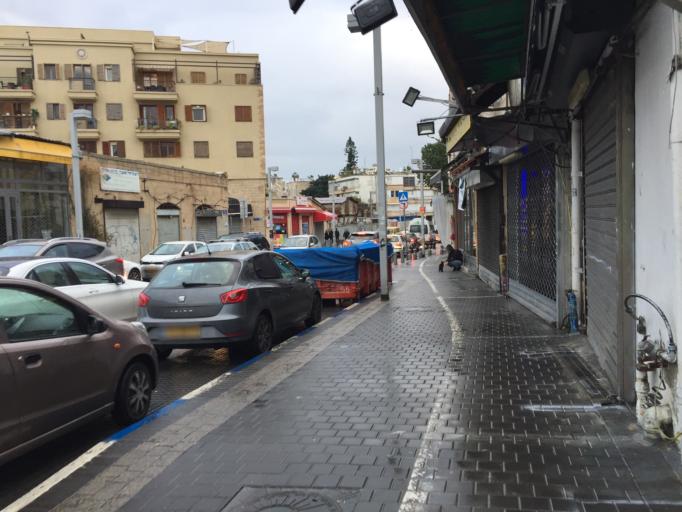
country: IL
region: Tel Aviv
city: Yafo
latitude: 32.0524
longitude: 34.7572
